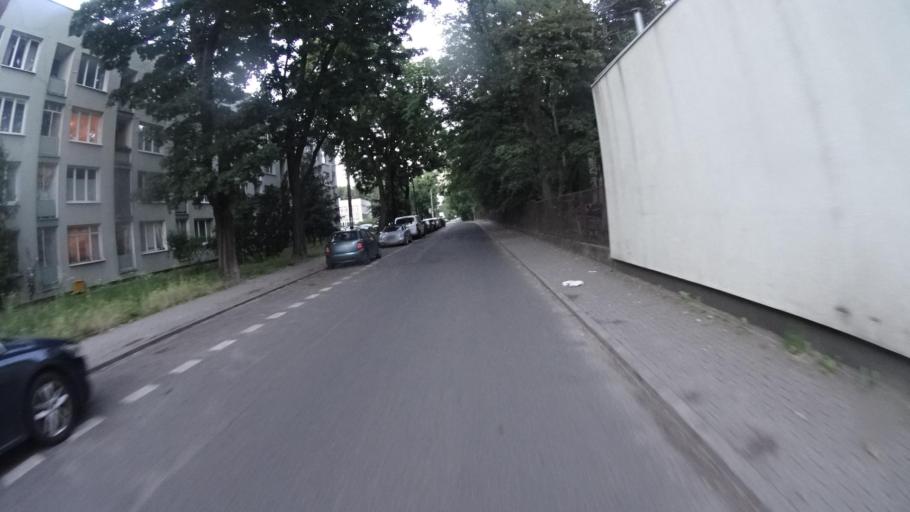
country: PL
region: Masovian Voivodeship
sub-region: Warszawa
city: Ochota
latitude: 52.2273
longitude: 20.9724
